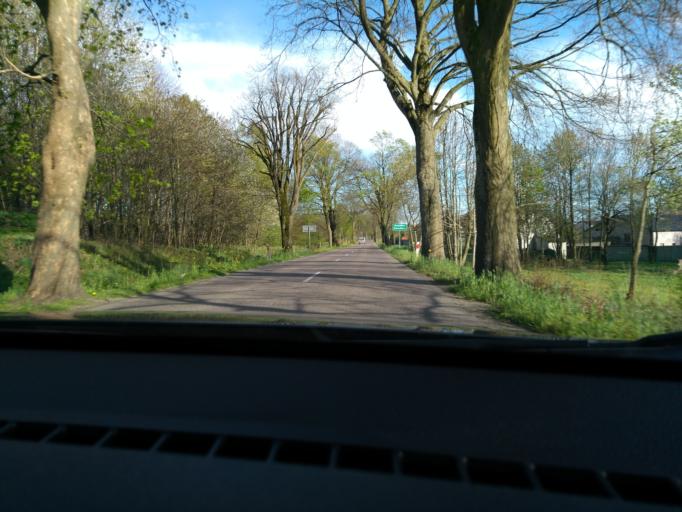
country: PL
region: Pomeranian Voivodeship
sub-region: Powiat kartuski
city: Suleczyno
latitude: 54.3360
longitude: 17.7654
